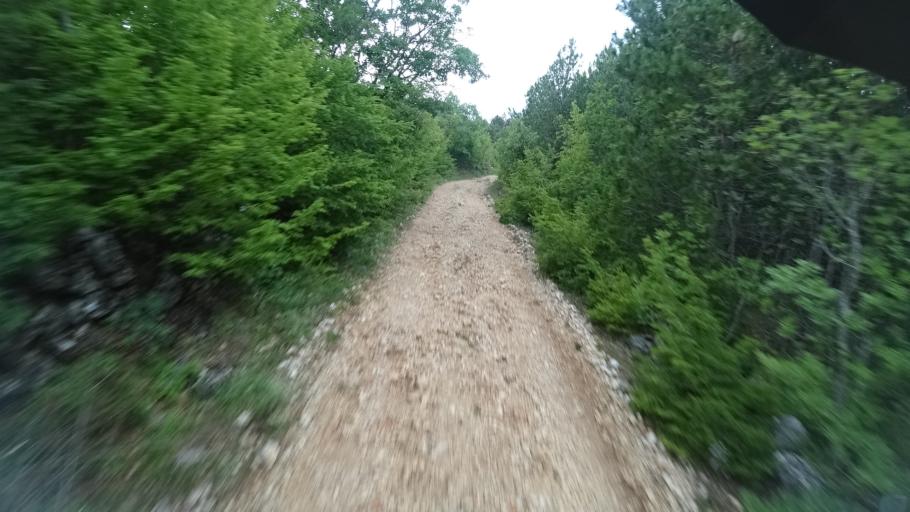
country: HR
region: Sibensko-Kniniska
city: Knin
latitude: 43.9840
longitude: 16.3435
